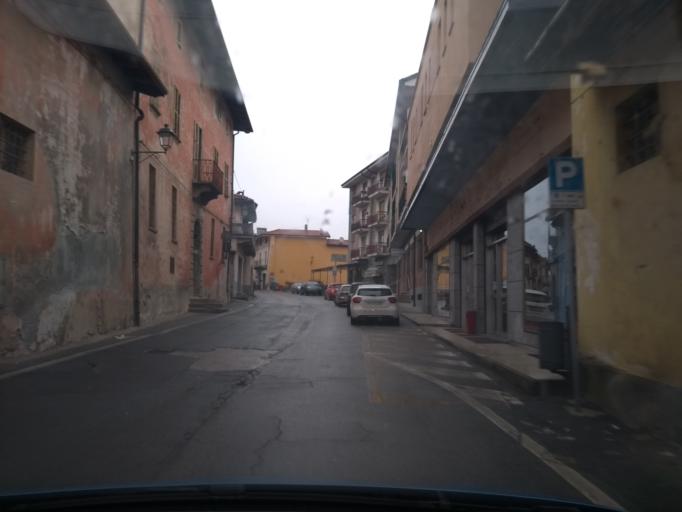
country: IT
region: Piedmont
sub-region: Provincia di Torino
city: Valperga
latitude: 45.3719
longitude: 7.6573
